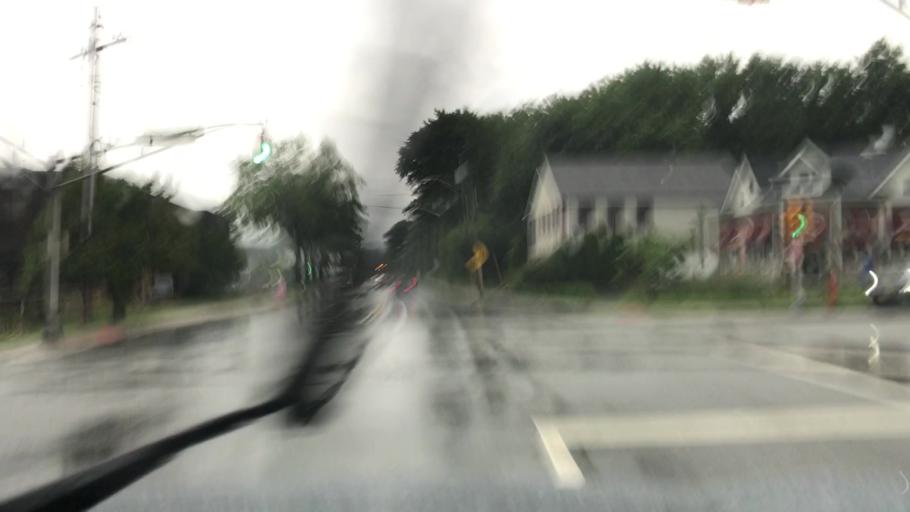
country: US
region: New Jersey
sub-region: Bergen County
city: Closter
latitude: 40.9710
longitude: -73.9593
